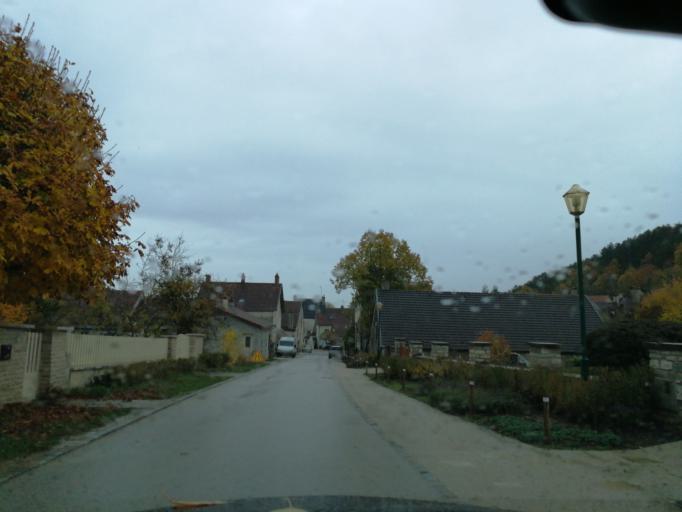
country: FR
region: Bourgogne
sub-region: Departement de la Cote-d'Or
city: Fleurey-sur-Ouche
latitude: 47.3238
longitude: 4.7915
